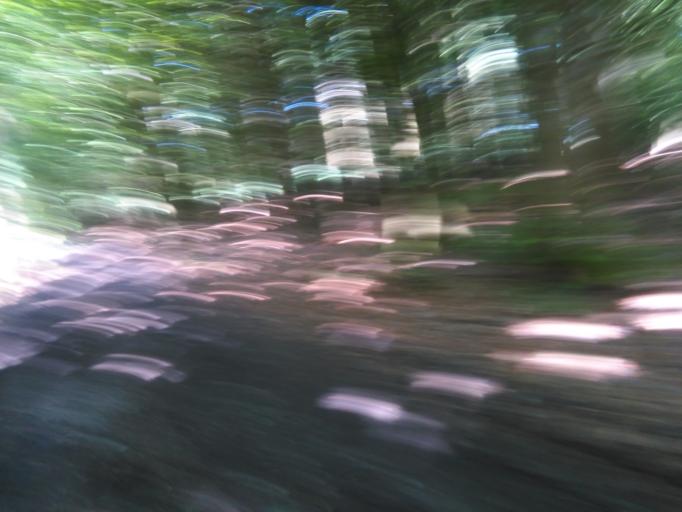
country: DK
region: Central Jutland
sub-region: Arhus Kommune
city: Solbjerg
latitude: 55.9544
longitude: 10.0412
